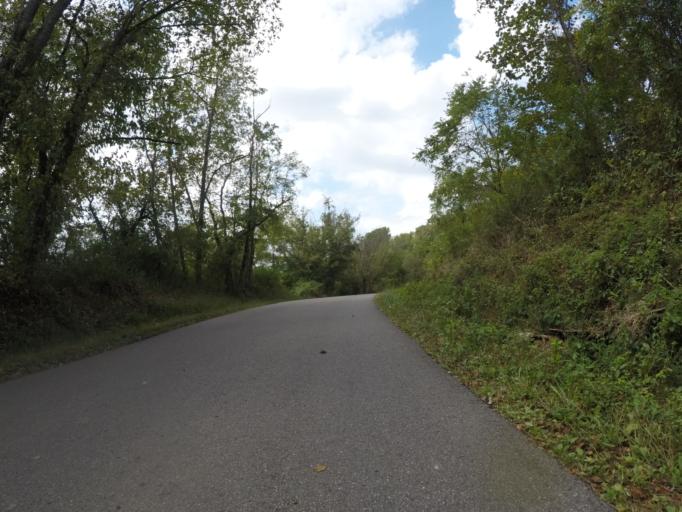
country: US
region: West Virginia
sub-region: Cabell County
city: Huntington
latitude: 38.4568
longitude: -82.4056
